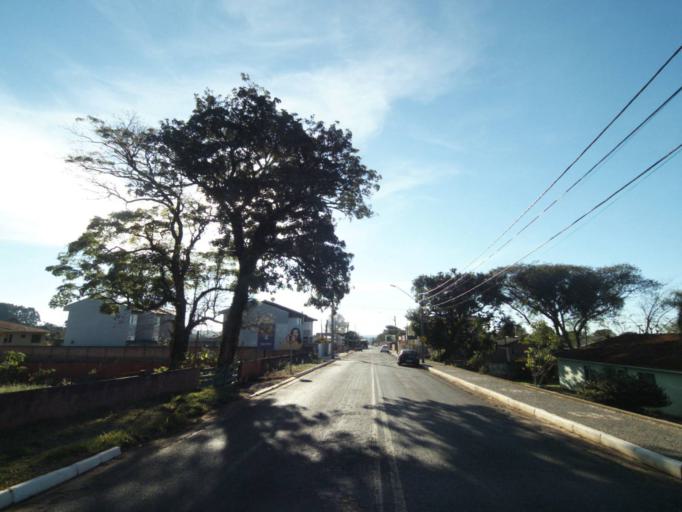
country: BR
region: Parana
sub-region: Tibagi
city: Tibagi
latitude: -24.5236
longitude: -50.4046
